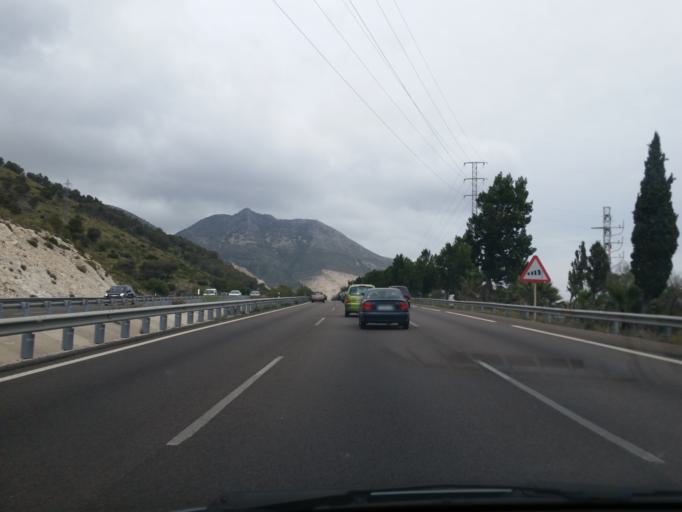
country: ES
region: Andalusia
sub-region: Provincia de Malaga
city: Benalmadena
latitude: 36.5928
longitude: -4.5796
